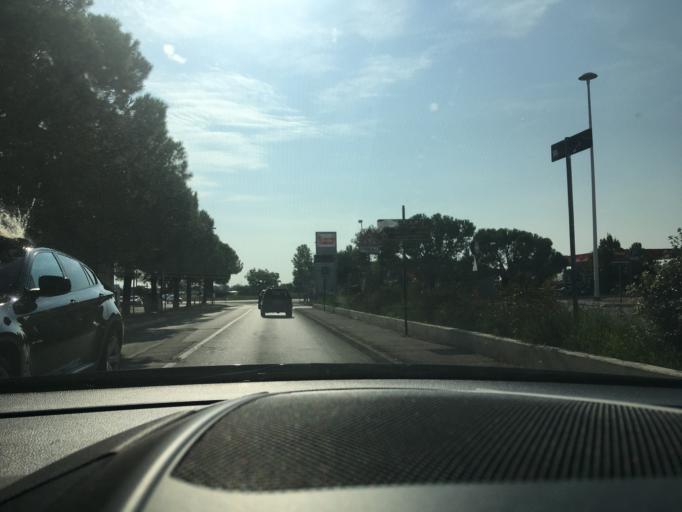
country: IT
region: Emilia-Romagna
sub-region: Forli-Cesena
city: Gatteo a Mare
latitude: 44.1566
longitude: 12.4325
